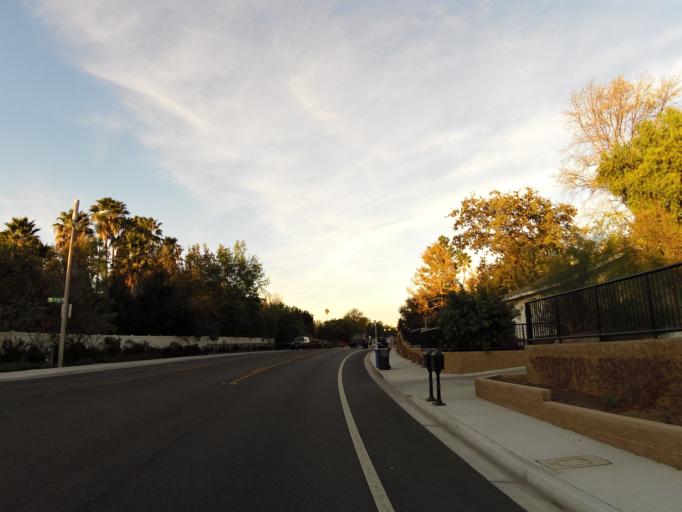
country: US
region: California
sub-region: Ventura County
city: Thousand Oaks
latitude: 34.1847
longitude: -118.8481
